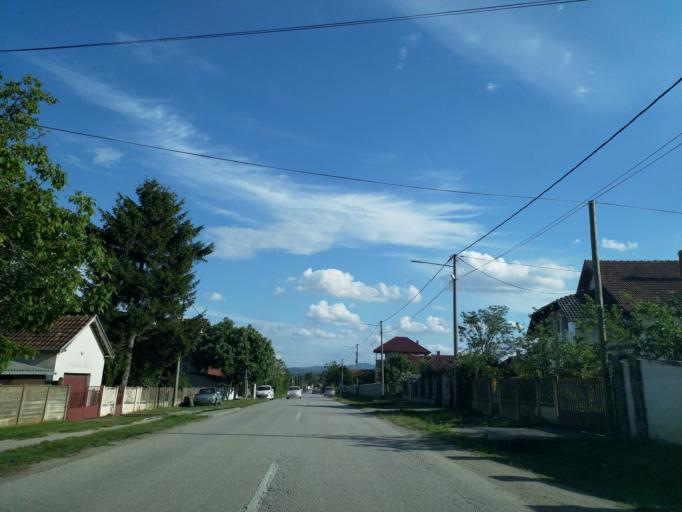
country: RS
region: Central Serbia
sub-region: Sumadijski Okrug
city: Lapovo
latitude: 44.1947
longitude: 21.0897
